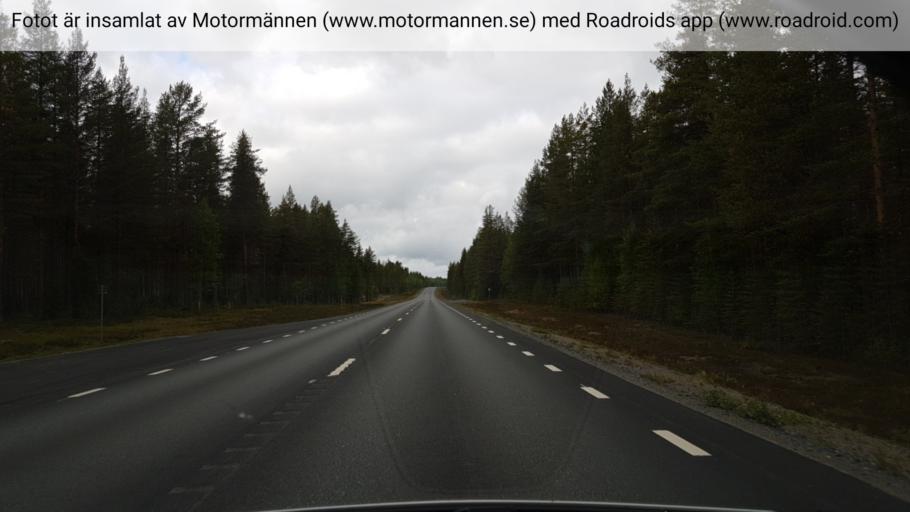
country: SE
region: Vaesterbotten
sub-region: Norsjo Kommun
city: Norsjoe
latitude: 64.9682
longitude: 19.7818
